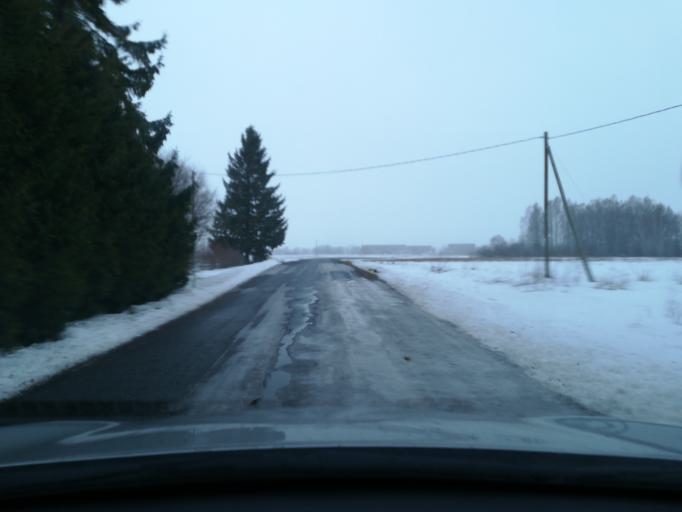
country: EE
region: Harju
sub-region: Raasiku vald
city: Raasiku
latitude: 59.3507
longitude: 25.2079
